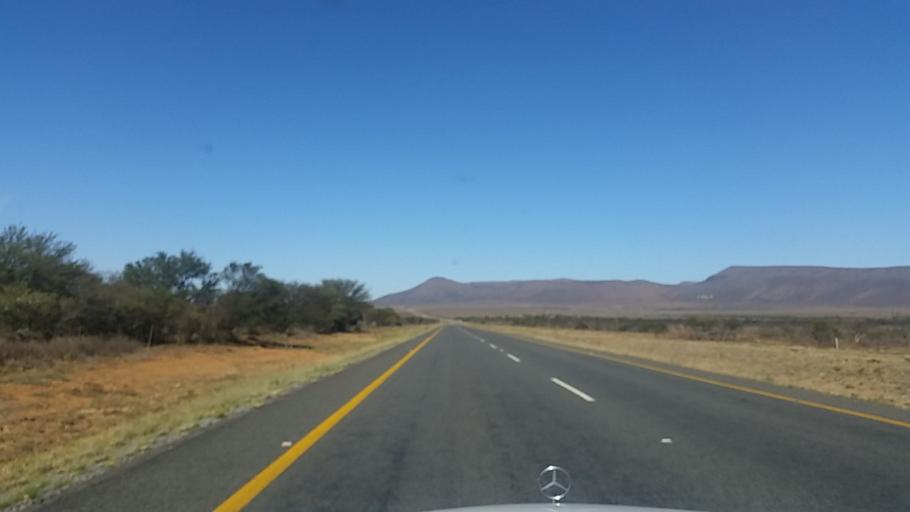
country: ZA
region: Eastern Cape
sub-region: Cacadu District Municipality
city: Graaff-Reinet
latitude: -31.9965
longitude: 24.6742
